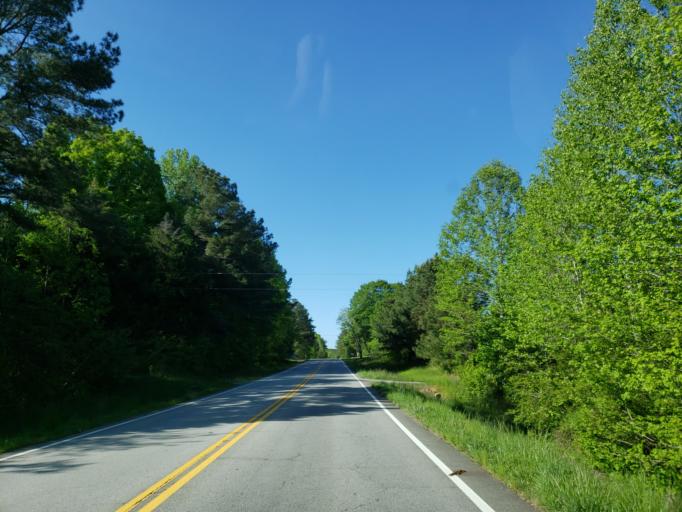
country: US
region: Georgia
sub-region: Haralson County
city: Tallapoosa
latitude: 33.8484
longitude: -85.2919
